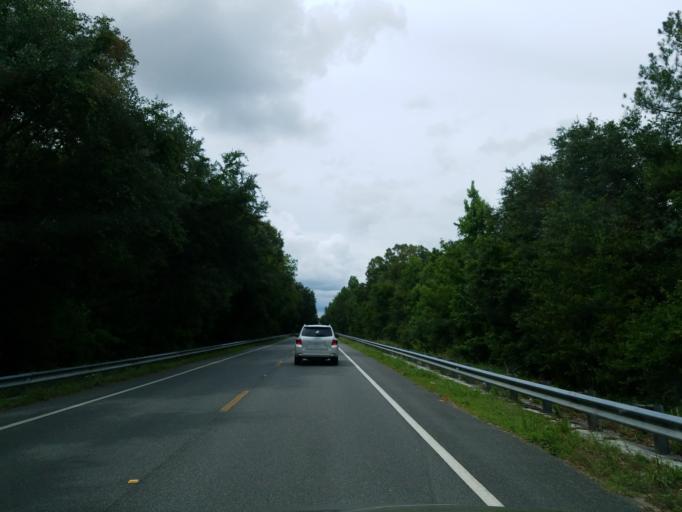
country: US
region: Florida
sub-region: Alachua County
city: High Springs
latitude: 29.9371
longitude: -82.5064
